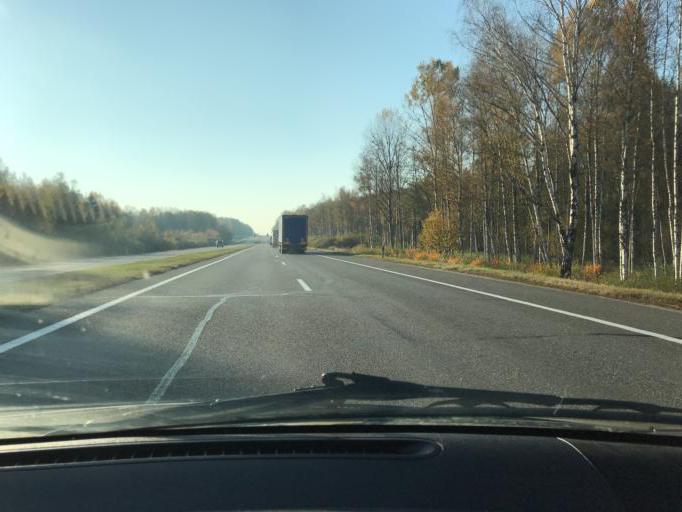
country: BY
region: Minsk
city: Krupki
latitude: 54.3016
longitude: 28.9623
